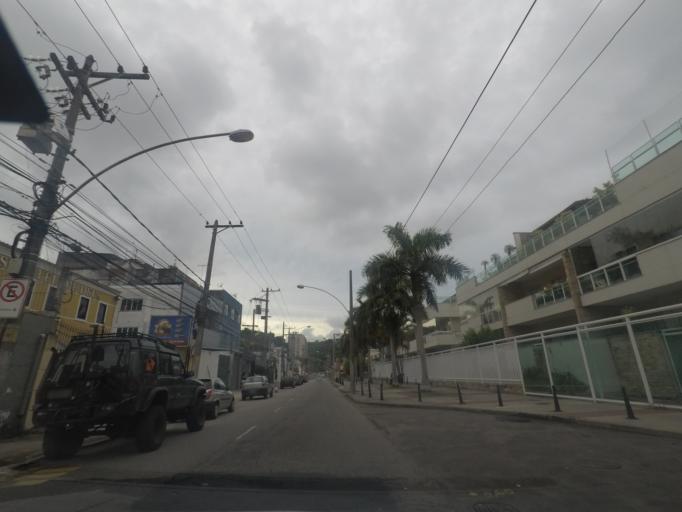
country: BR
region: Rio de Janeiro
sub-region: Rio De Janeiro
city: Rio de Janeiro
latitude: -23.0094
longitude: -43.2995
